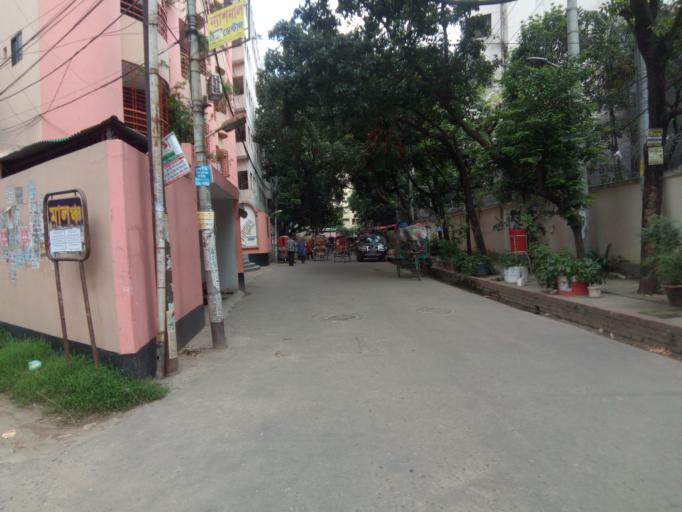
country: BD
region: Dhaka
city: Paltan
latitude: 23.7459
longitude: 90.3999
